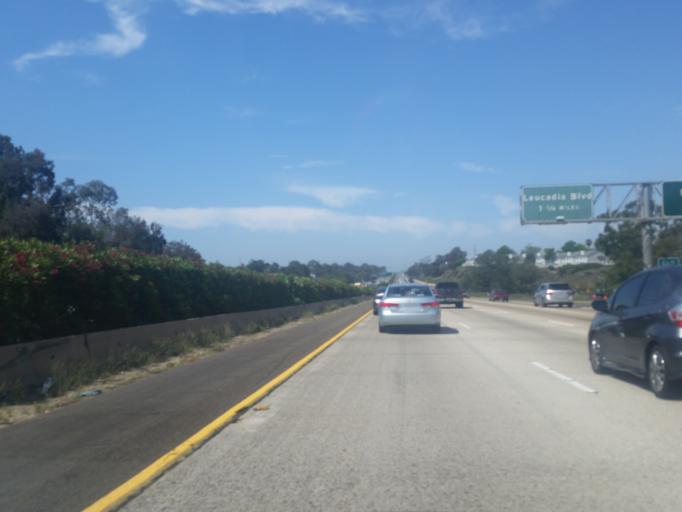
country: US
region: California
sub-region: San Diego County
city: Encinitas
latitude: 33.0454
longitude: -117.2862
